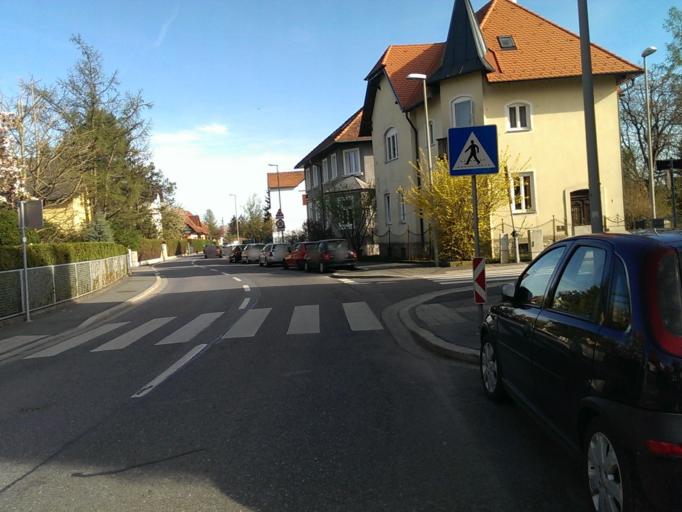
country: AT
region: Styria
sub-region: Graz Stadt
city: Graz
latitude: 47.0447
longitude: 15.4532
